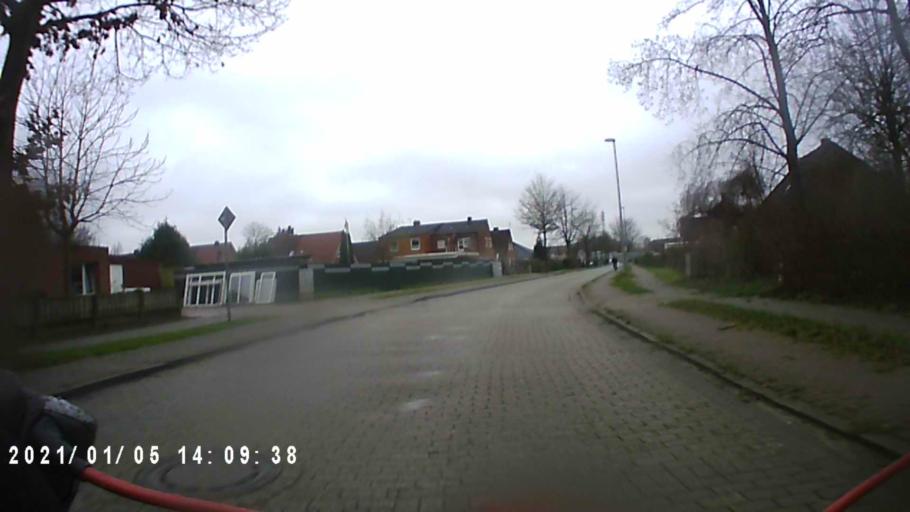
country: DE
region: Lower Saxony
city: Weener
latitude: 53.1665
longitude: 7.3383
